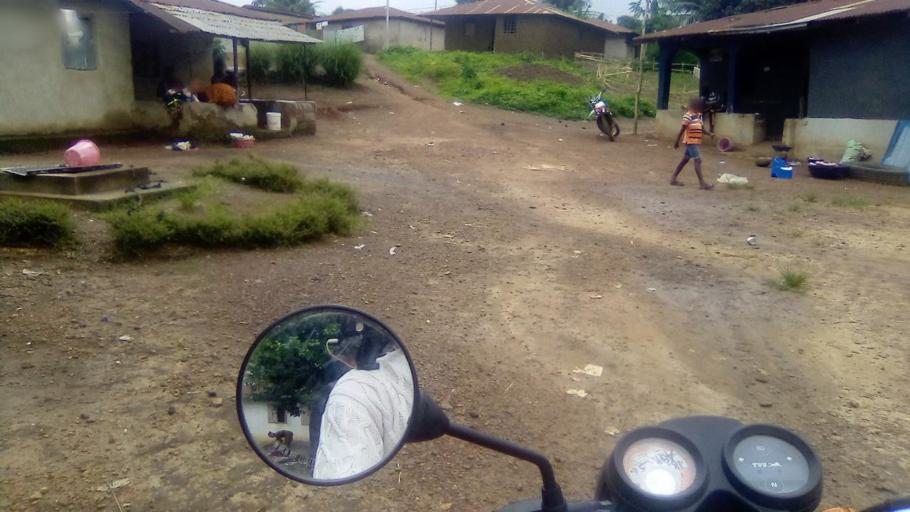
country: SL
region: Southern Province
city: Tongole
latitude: 7.4320
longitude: -11.8437
